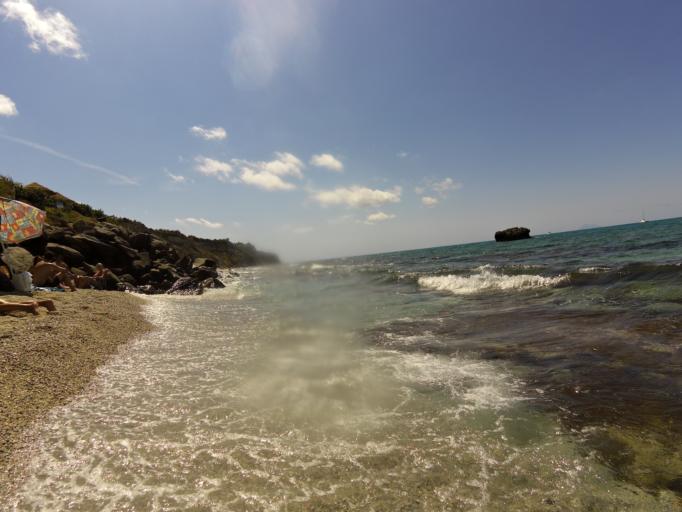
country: IT
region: Calabria
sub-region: Provincia di Vibo-Valentia
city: Santa Domenica
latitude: 38.6705
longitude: 15.8687
